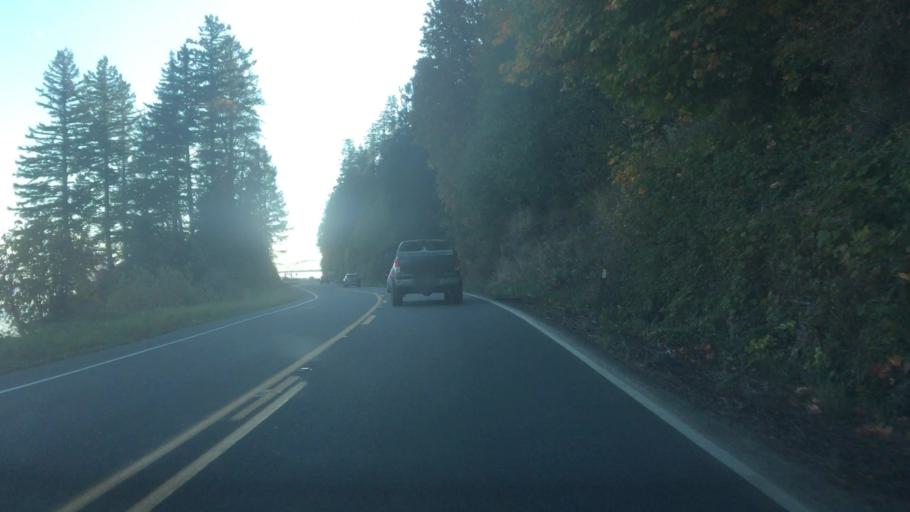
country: US
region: Oregon
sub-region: Clatsop County
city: Astoria
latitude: 46.2472
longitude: -123.8679
